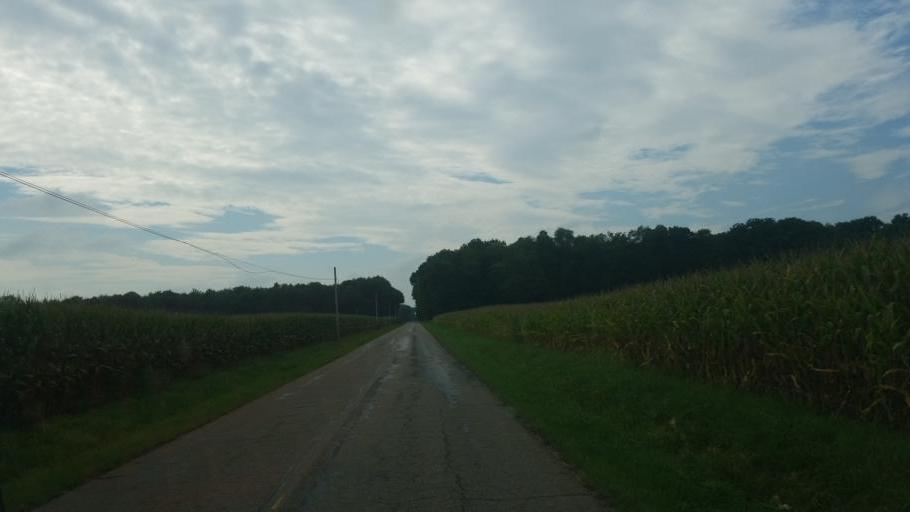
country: US
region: Ohio
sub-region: Wayne County
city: Wooster
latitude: 40.9011
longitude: -81.9565
